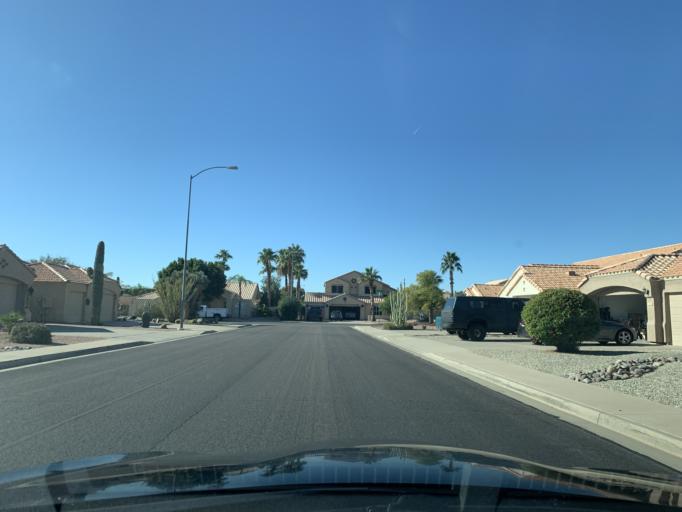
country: US
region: Arizona
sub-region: Pinal County
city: Apache Junction
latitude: 33.3849
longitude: -111.6250
